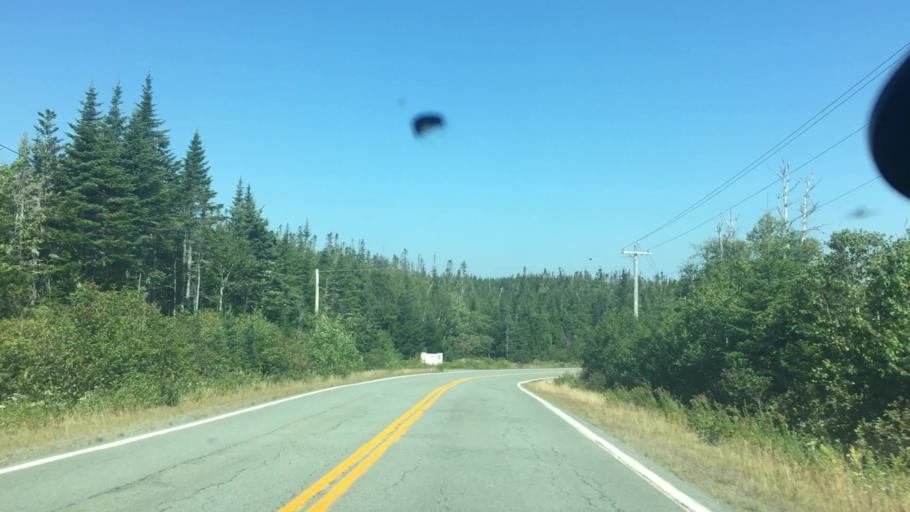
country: CA
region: Nova Scotia
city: Antigonish
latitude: 45.0119
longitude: -62.1053
